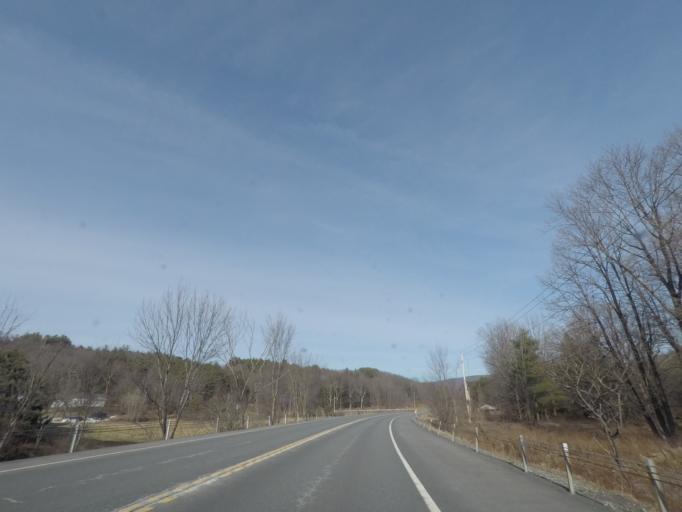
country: US
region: Massachusetts
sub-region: Berkshire County
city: Williamstown
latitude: 42.7403
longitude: -73.3592
